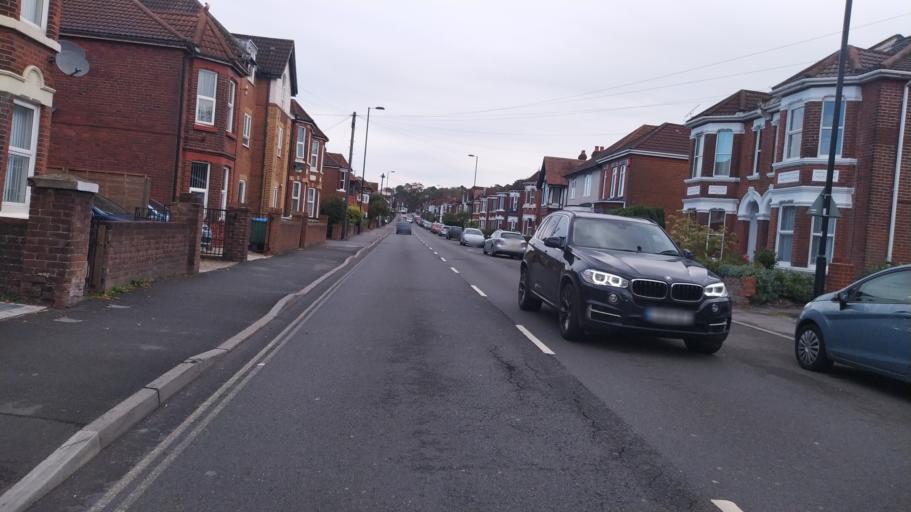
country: GB
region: England
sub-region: Southampton
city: Southampton
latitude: 50.9191
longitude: -1.3749
